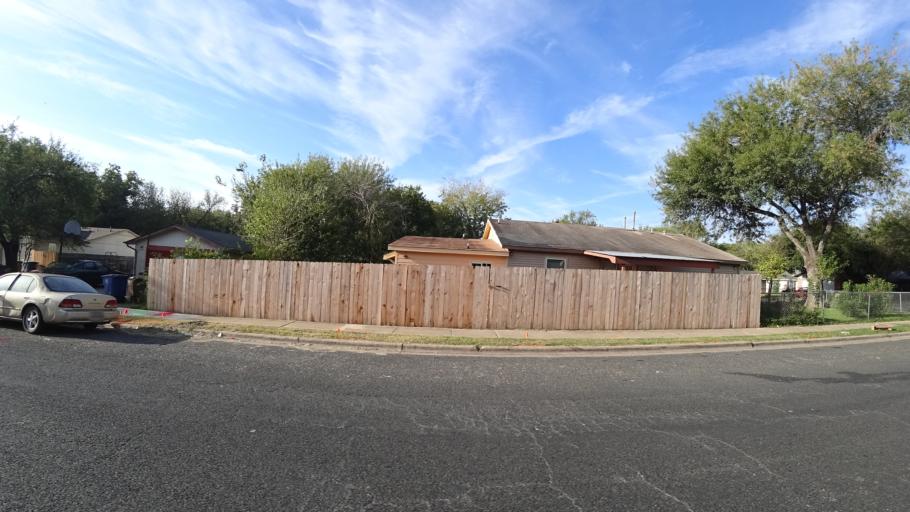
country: US
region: Texas
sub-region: Travis County
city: Onion Creek
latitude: 30.1915
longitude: -97.7475
